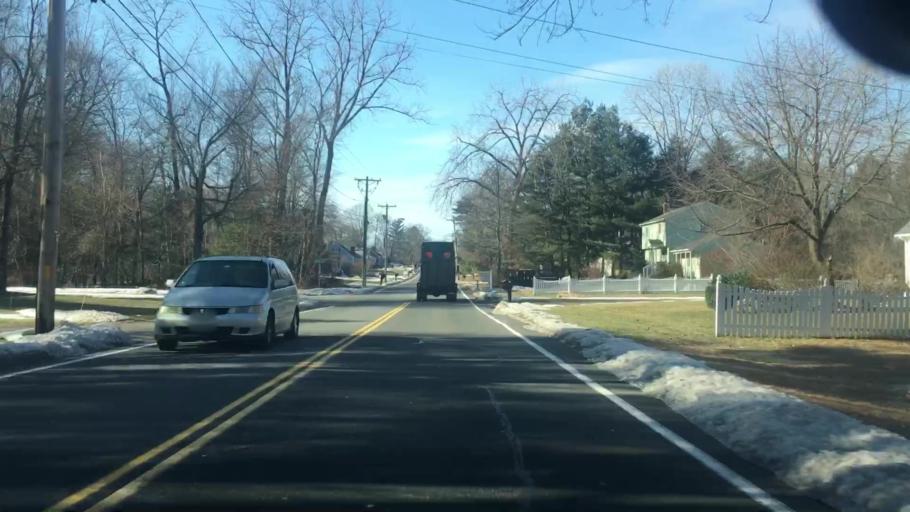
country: US
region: Massachusetts
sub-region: Hampden County
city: East Longmeadow
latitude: 42.0547
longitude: -72.5063
